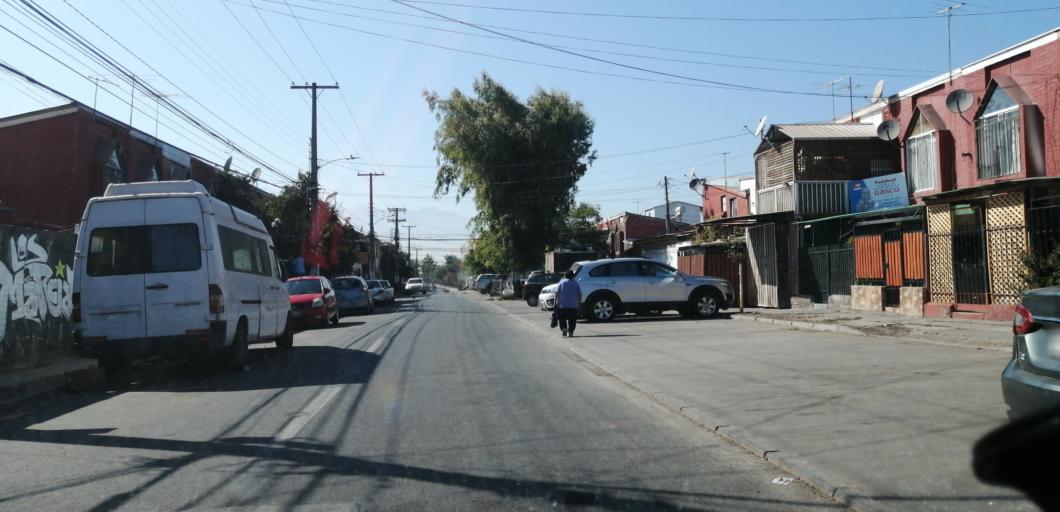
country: CL
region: Santiago Metropolitan
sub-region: Provincia de Santiago
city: Lo Prado
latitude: -33.4464
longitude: -70.7656
